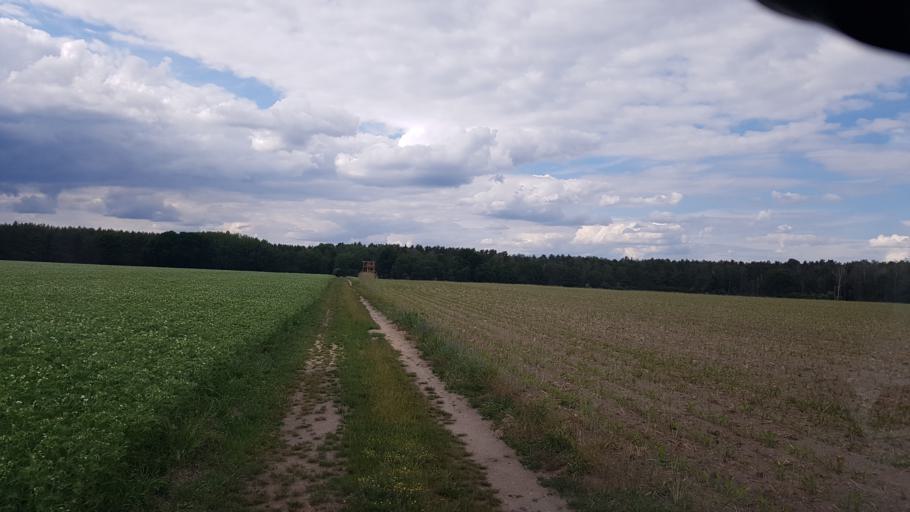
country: DE
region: Brandenburg
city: Finsterwalde
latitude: 51.6139
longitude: 13.6612
